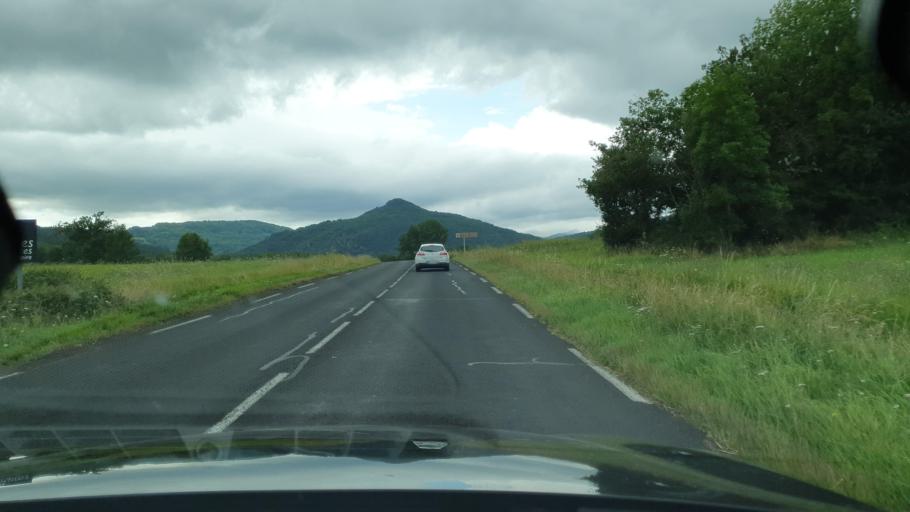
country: FR
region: Auvergne
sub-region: Departement du Puy-de-Dome
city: Aydat
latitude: 45.5747
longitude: 3.0250
